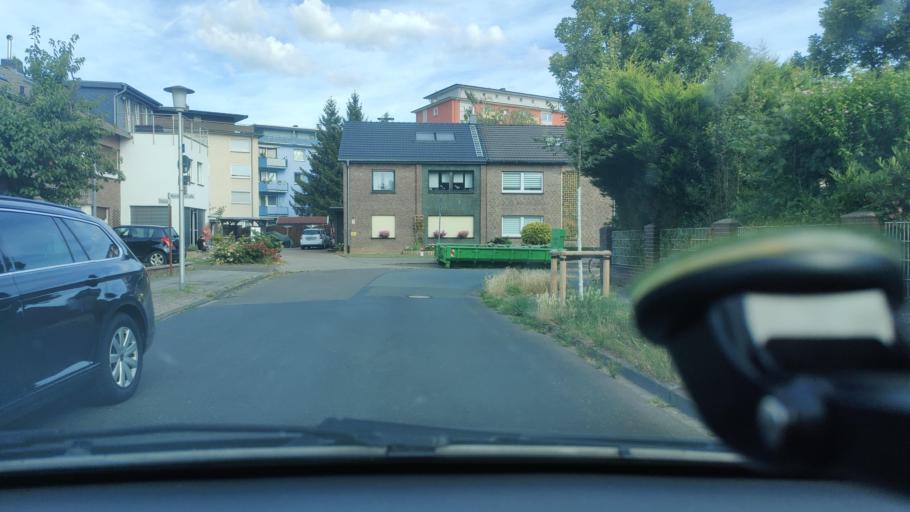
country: DE
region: North Rhine-Westphalia
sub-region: Regierungsbezirk Dusseldorf
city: Kamp-Lintfort
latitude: 51.5011
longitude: 6.5608
